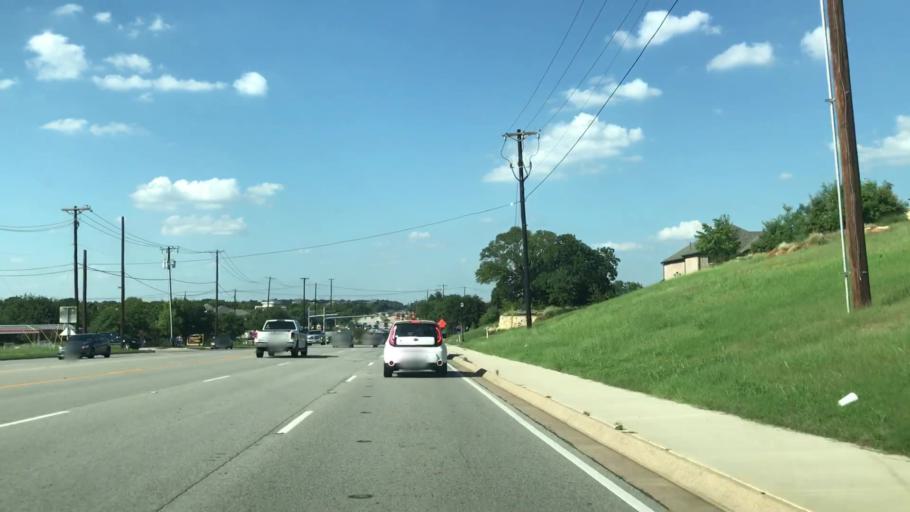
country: US
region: Texas
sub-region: Tarrant County
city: Southlake
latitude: 32.9346
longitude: -97.1857
